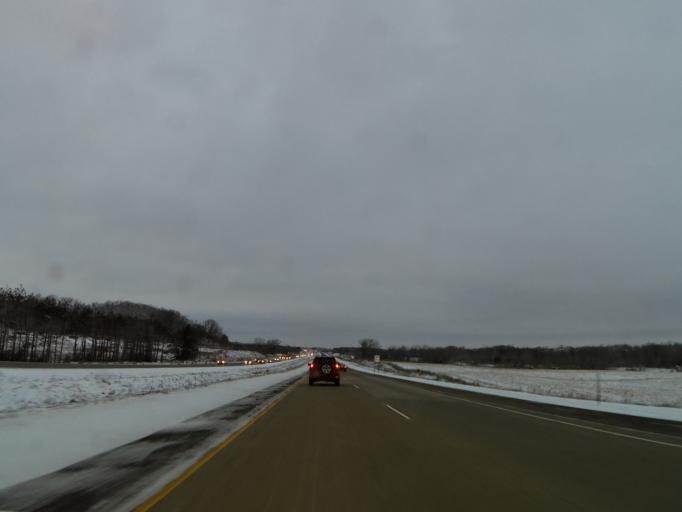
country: US
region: Wisconsin
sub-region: Saint Croix County
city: Roberts
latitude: 44.9606
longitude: -92.5734
